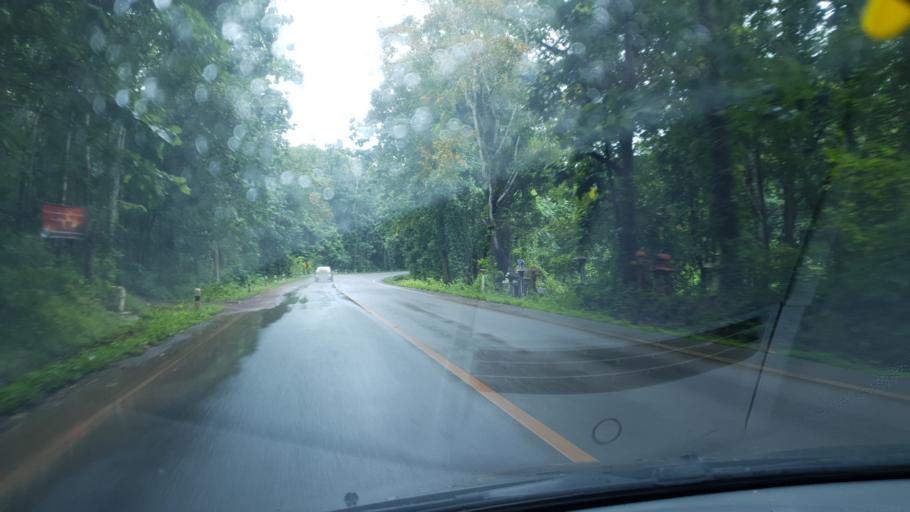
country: TH
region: Mae Hong Son
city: Pa Pae
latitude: 18.2320
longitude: 97.9449
